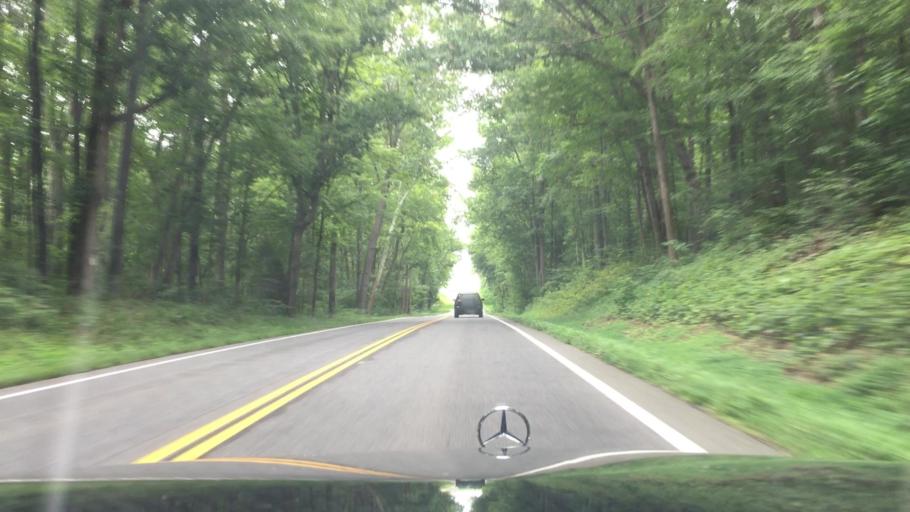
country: US
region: Virginia
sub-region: Nottoway County
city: Crewe
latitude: 37.2742
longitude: -78.1707
